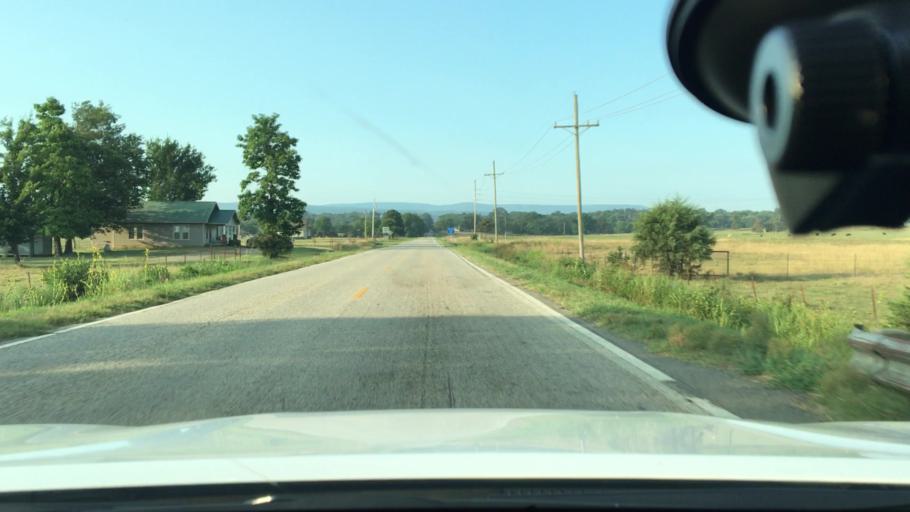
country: US
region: Arkansas
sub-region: Logan County
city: Paris
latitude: 35.3248
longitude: -93.6322
